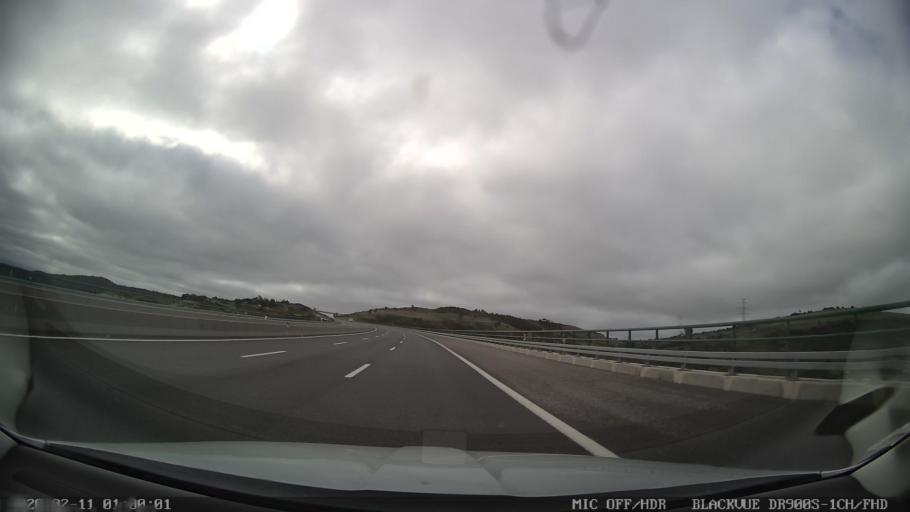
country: PT
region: Lisbon
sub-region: Arruda Dos Vinhos
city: Arruda dos Vinhos
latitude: 38.9355
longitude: -9.0733
